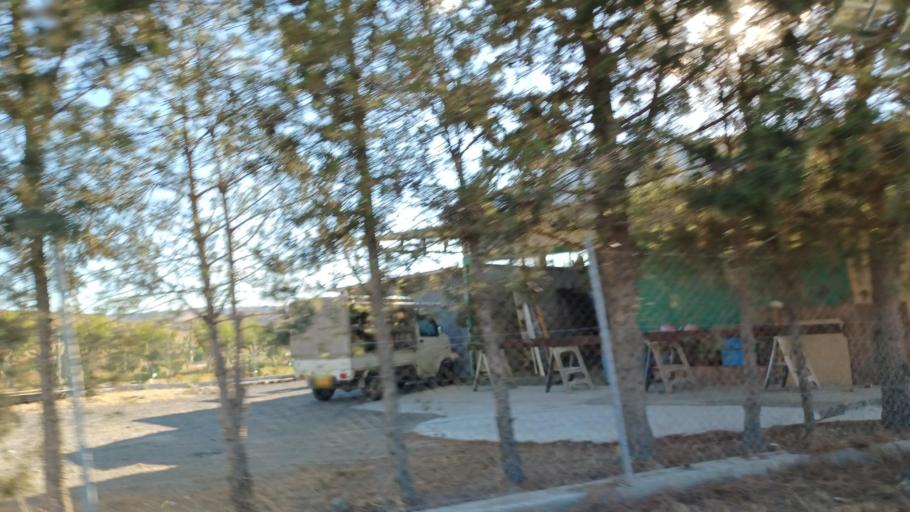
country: CY
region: Larnaka
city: Troulloi
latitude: 35.0119
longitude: 33.6348
